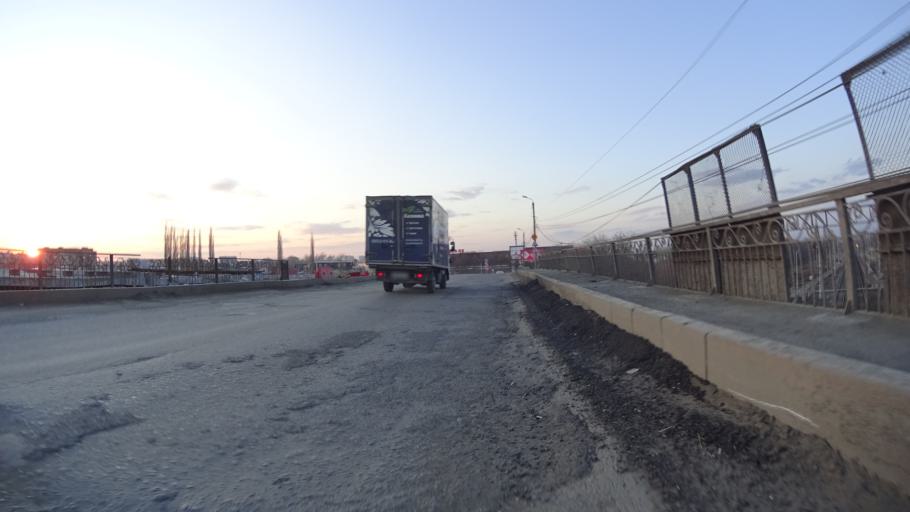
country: RU
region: Chelyabinsk
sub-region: Gorod Chelyabinsk
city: Chelyabinsk
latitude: 55.1162
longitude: 61.3857
